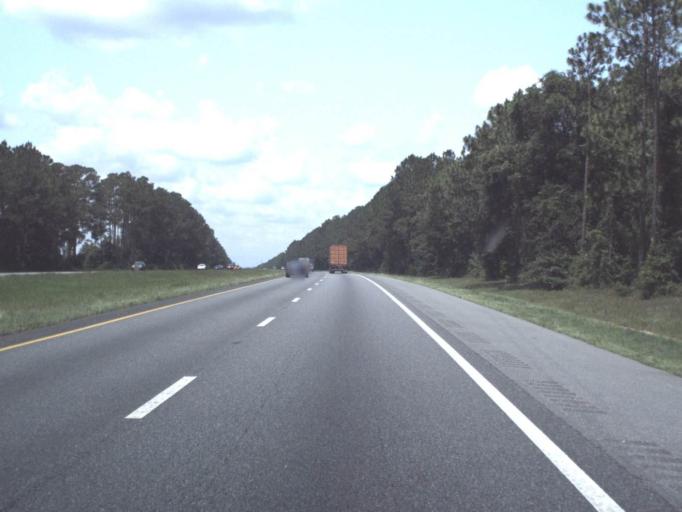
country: US
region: Florida
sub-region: Baker County
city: Macclenny
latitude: 30.2779
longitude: -82.0692
